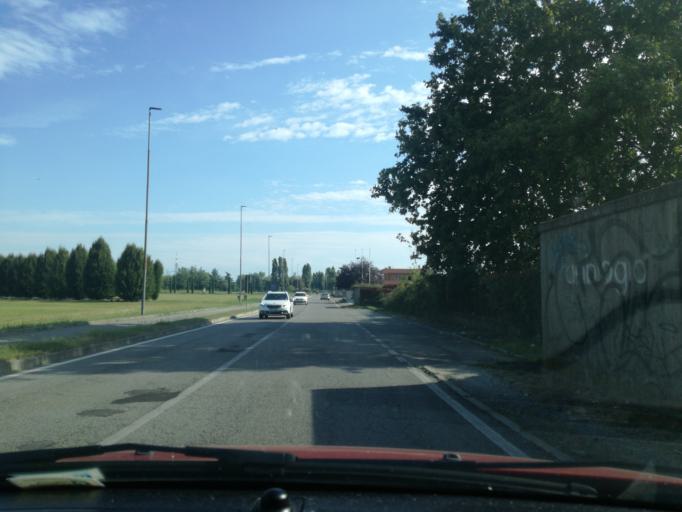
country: IT
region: Lombardy
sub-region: Provincia di Monza e Brianza
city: Velasca
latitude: 45.6455
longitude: 9.3453
